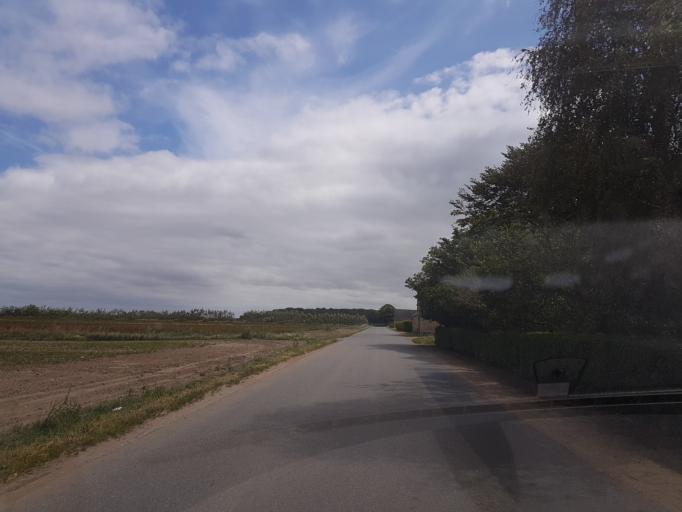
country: DK
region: South Denmark
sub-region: Nordfyns Kommune
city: Bogense
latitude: 55.5445
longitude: 10.0426
